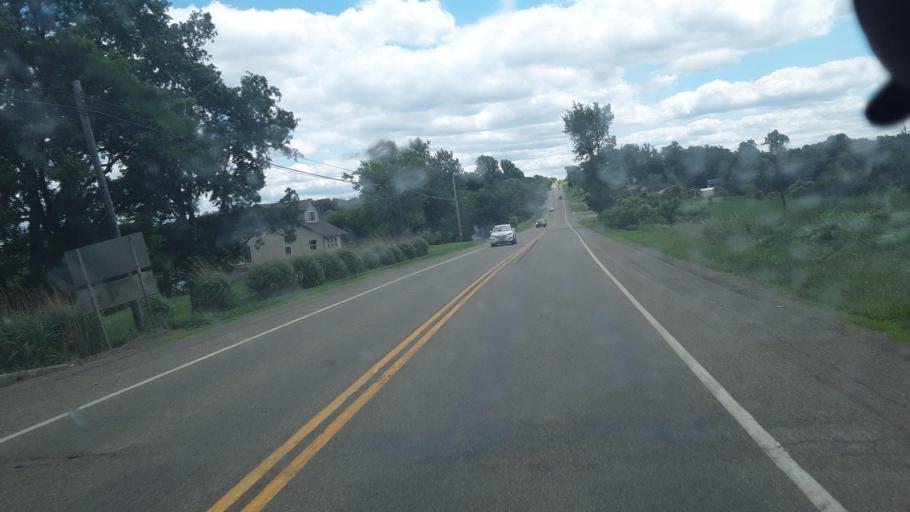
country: US
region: Pennsylvania
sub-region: Butler County
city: Prospect
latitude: 40.9559
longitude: -80.1548
